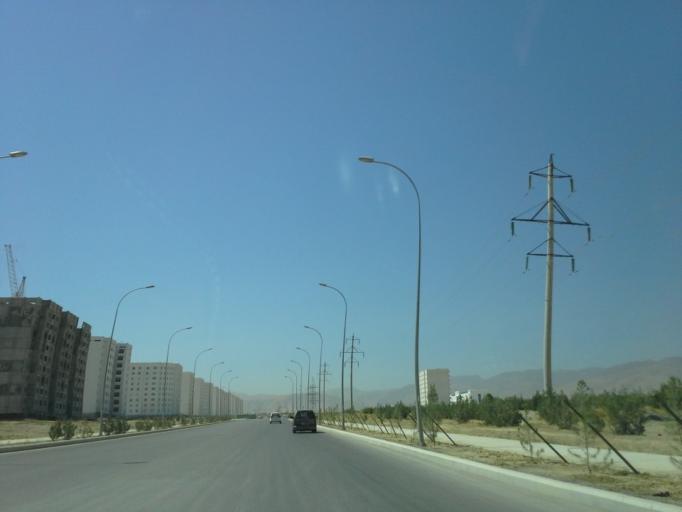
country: TM
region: Ahal
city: Ashgabat
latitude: 37.8987
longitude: 58.4057
